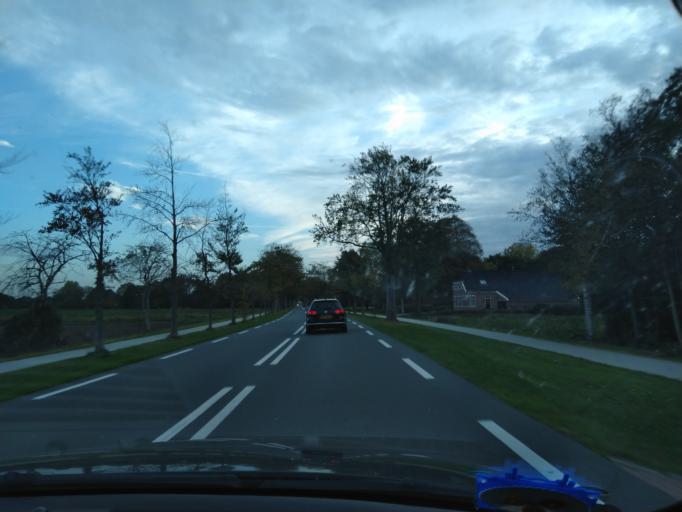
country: NL
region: Drenthe
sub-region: Gemeente Tynaarlo
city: Vries
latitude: 53.0400
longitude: 6.5712
